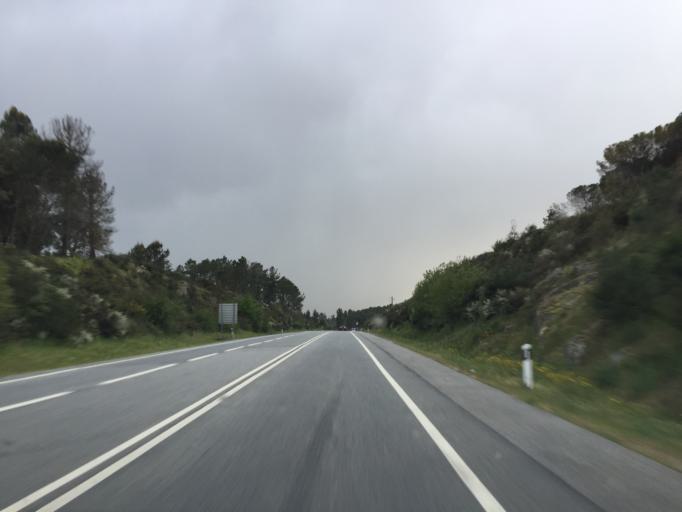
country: PT
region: Viseu
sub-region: Viseu
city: Viseu
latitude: 40.6099
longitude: -7.9614
